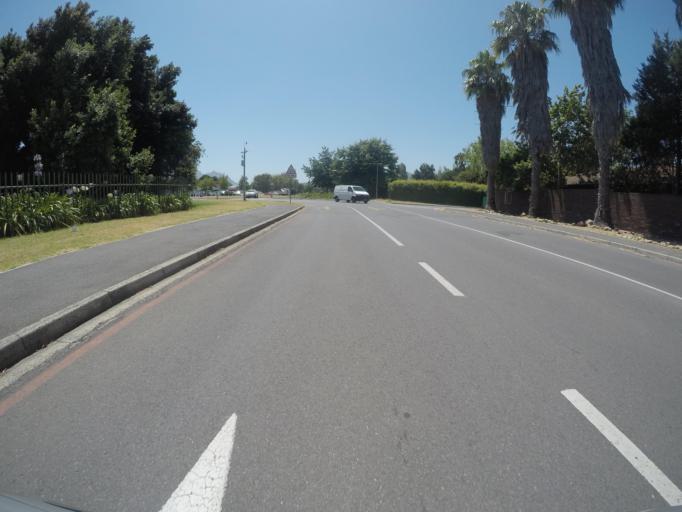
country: ZA
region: Western Cape
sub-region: Cape Winelands District Municipality
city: Stellenbosch
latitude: -33.9451
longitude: 18.8508
